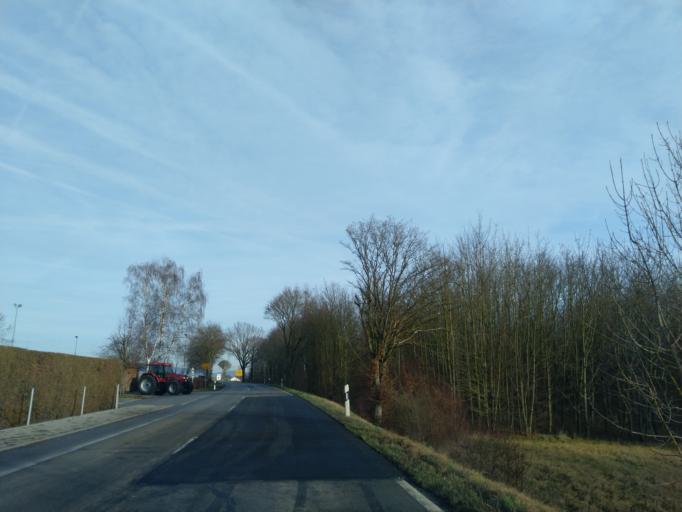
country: DE
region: Bavaria
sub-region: Lower Bavaria
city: Buchhofen
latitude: 48.6973
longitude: 12.9360
